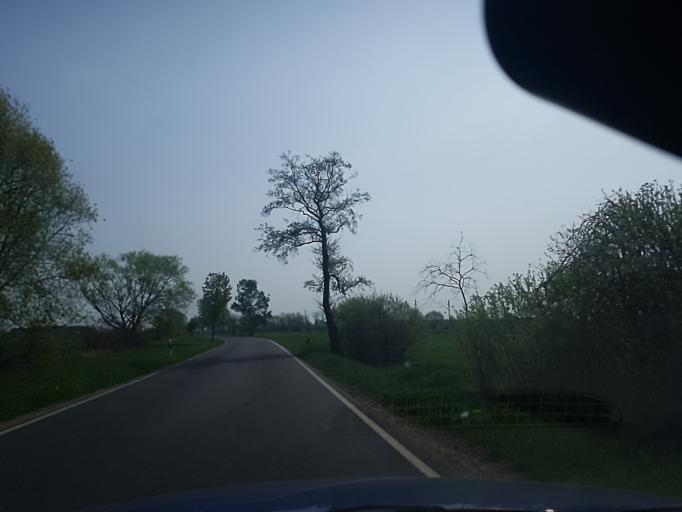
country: DE
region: Brandenburg
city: Falkenberg
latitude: 51.5836
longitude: 13.1850
